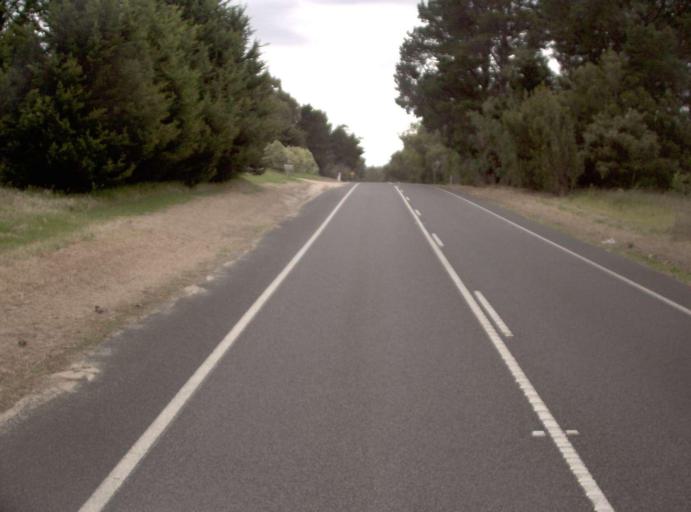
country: AU
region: Victoria
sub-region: Wellington
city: Sale
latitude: -38.2005
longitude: 147.0756
